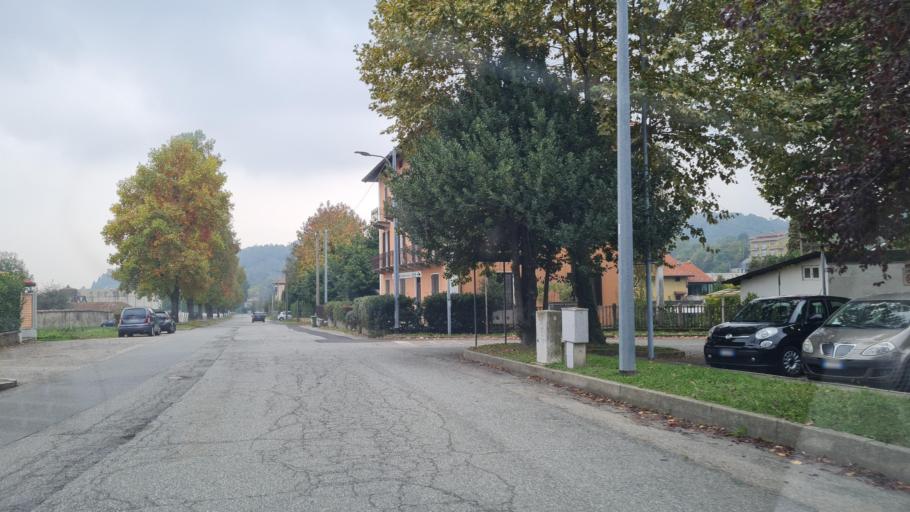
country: IT
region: Piedmont
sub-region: Provincia di Biella
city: Tollegno
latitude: 45.5872
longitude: 8.0528
